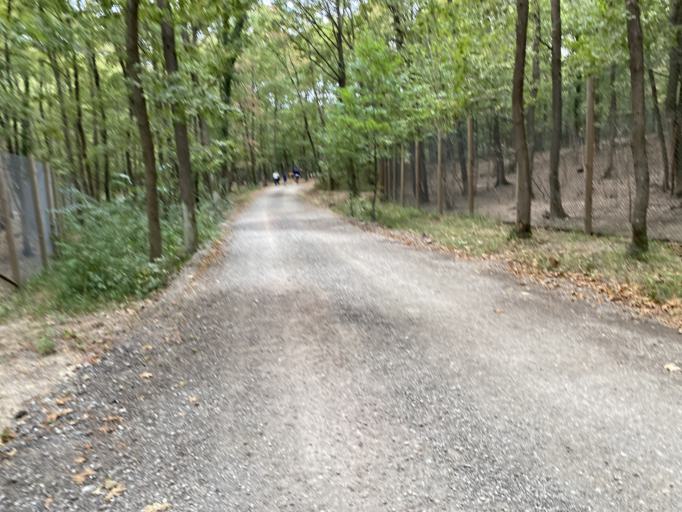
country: TR
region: Kocaeli
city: Derbent
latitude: 40.7377
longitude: 30.1633
